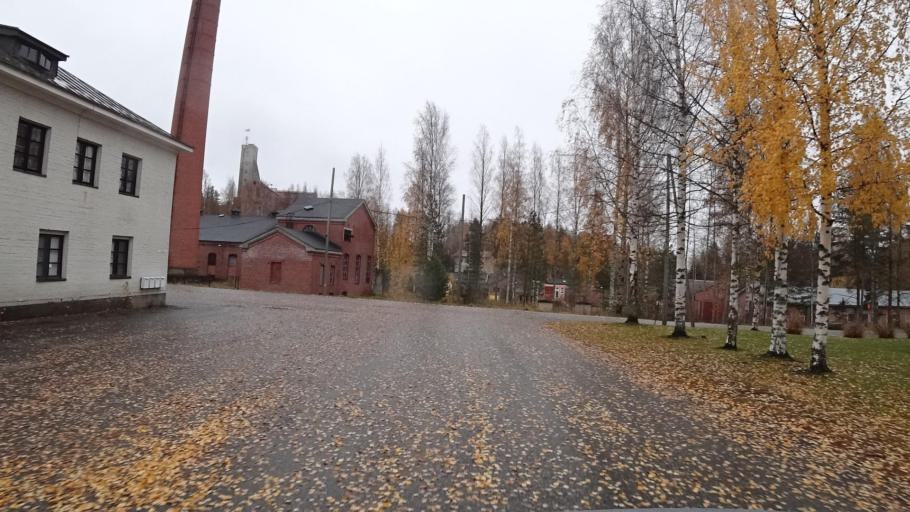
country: FI
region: North Karelia
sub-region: Joensuu
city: Outokumpu
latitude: 62.7319
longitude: 29.0018
